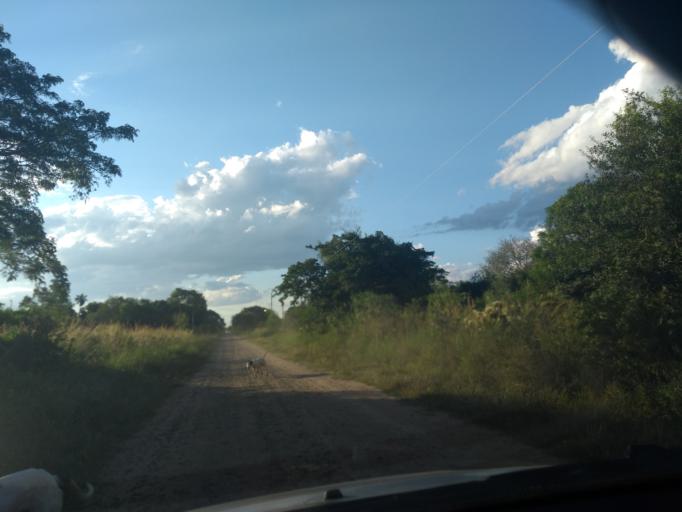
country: AR
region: Chaco
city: Colonia Benitez
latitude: -27.3930
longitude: -58.9391
